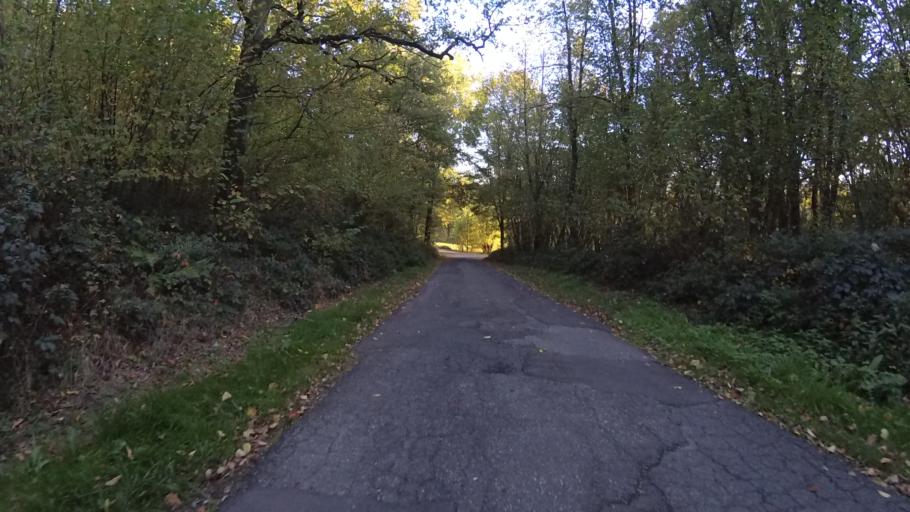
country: DE
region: Saarland
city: Sankt Wendel
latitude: 49.4513
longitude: 7.1775
